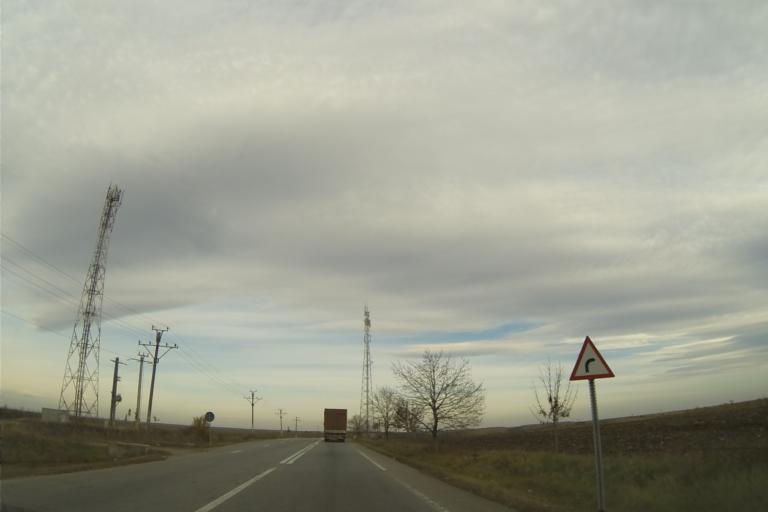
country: RO
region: Olt
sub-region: Comuna Scornicesti
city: Negreni
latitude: 44.5653
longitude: 24.5823
